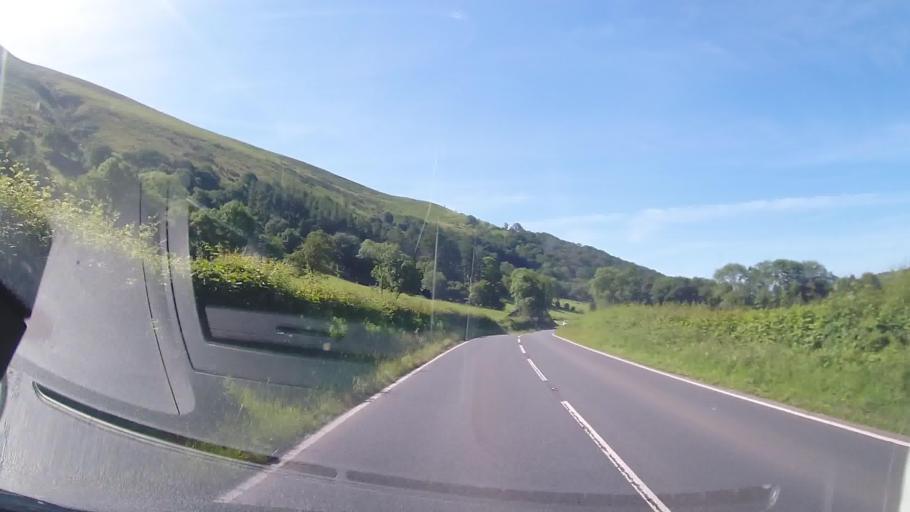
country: GB
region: Wales
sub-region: Gwynedd
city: Corris
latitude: 52.6916
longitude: -3.6838
